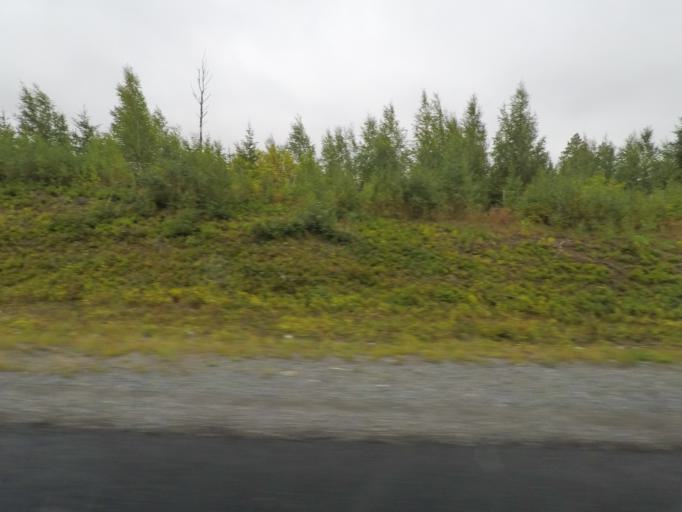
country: FI
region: Northern Savo
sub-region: Kuopio
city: Kuopio
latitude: 62.7759
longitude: 27.5891
